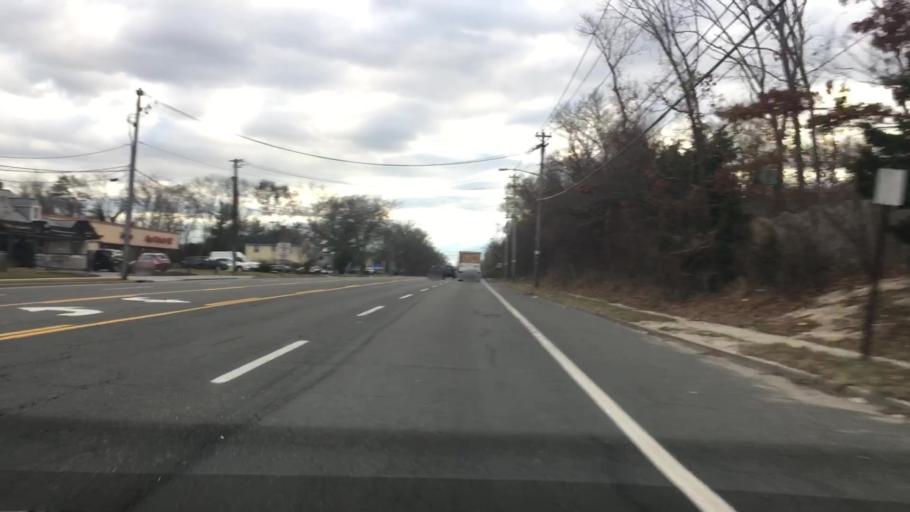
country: US
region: New York
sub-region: Suffolk County
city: Commack
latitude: 40.8141
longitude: -73.2941
